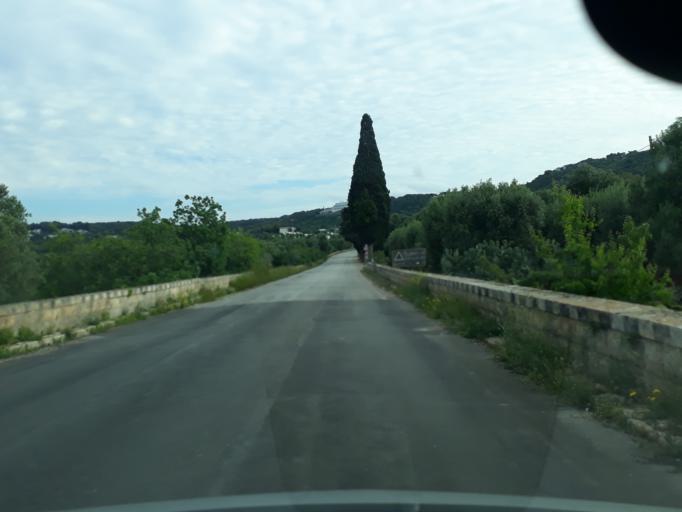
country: IT
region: Apulia
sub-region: Provincia di Brindisi
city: Ostuni
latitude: 40.7449
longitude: 17.5589
